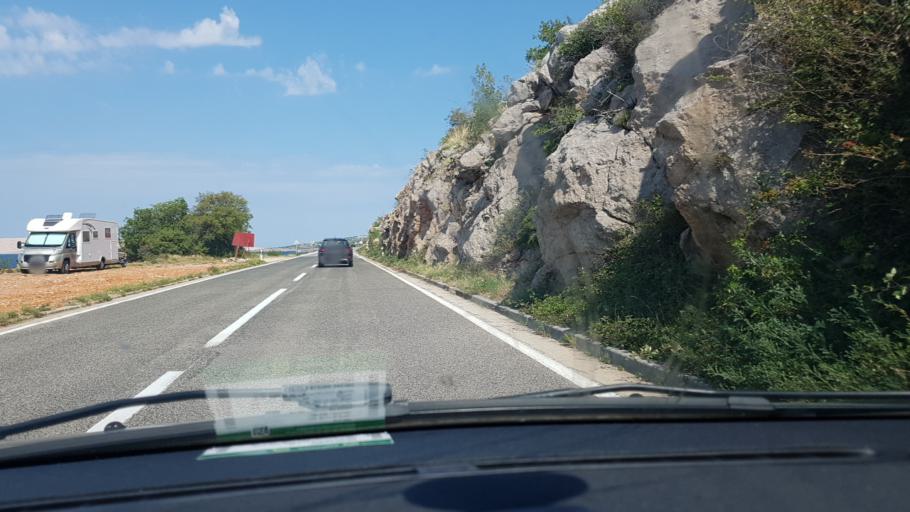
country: HR
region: Licko-Senjska
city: Karlobag
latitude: 44.5446
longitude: 15.0500
